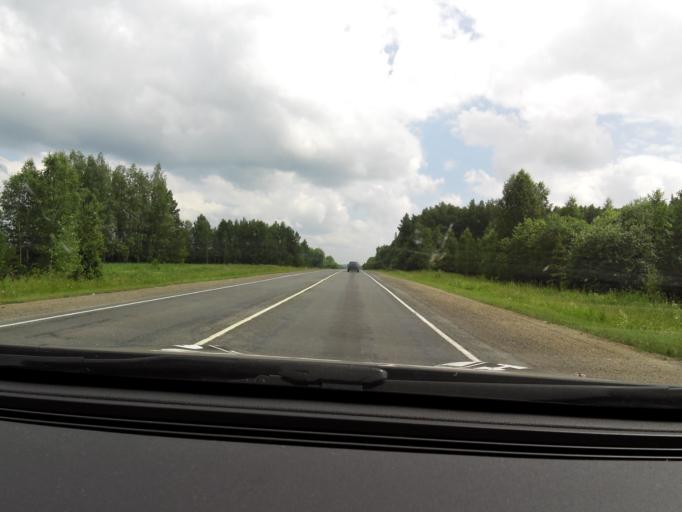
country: RU
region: Sverdlovsk
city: Achit
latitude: 56.8711
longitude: 57.6588
